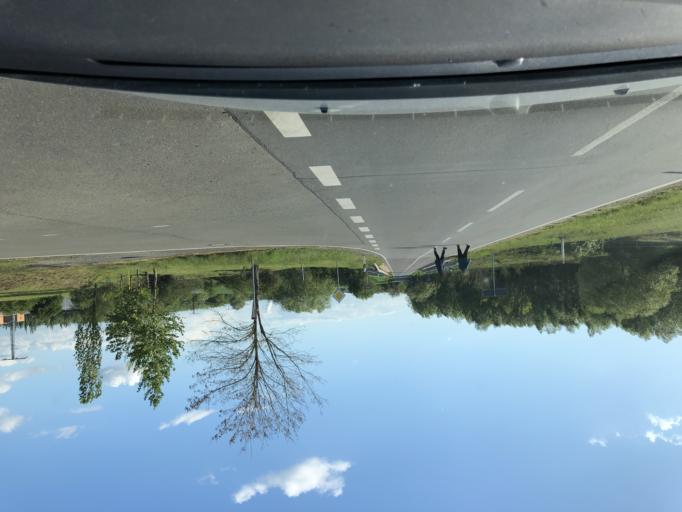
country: DE
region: Saxony
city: Regis-Breitingen
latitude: 51.0980
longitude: 12.4352
